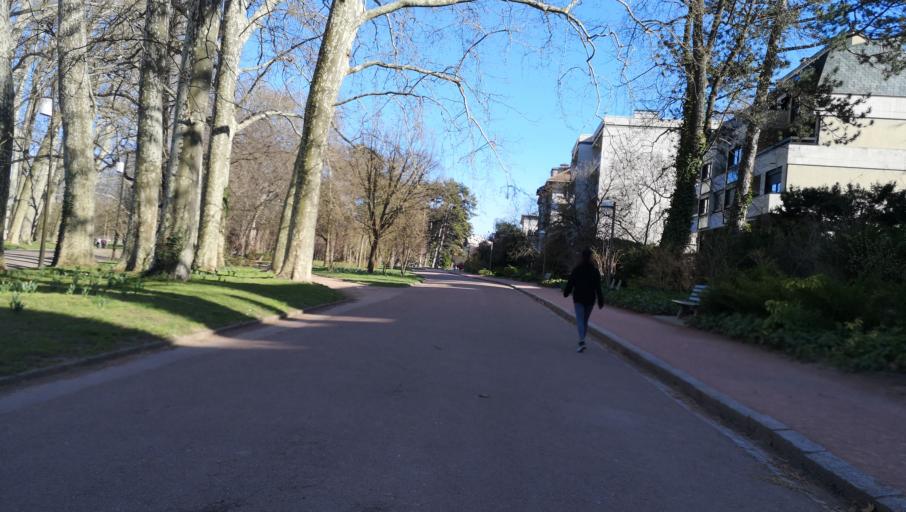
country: FR
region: Rhone-Alpes
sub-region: Departement du Rhone
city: Caluire-et-Cuire
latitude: 45.7758
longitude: 4.8479
